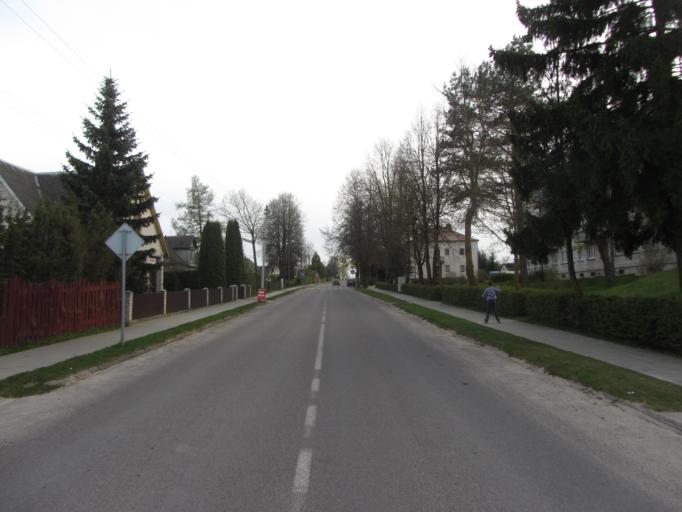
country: LT
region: Utenos apskritis
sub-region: Utena
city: Utena
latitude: 55.7386
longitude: 25.8343
